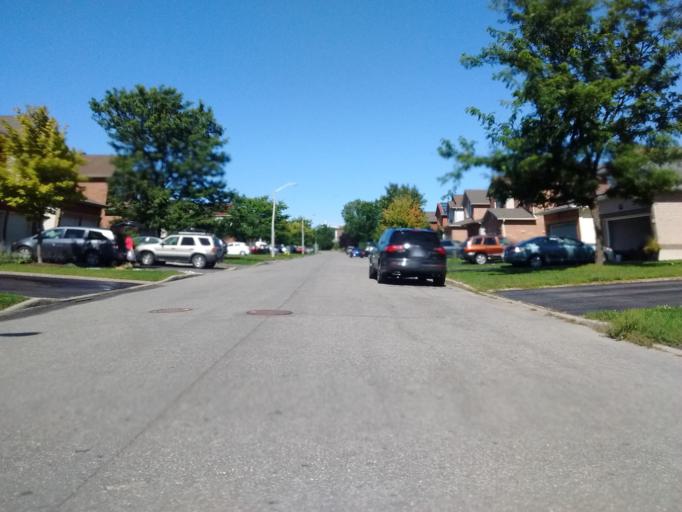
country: CA
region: Ontario
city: Ottawa
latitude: 45.4375
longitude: -75.6336
